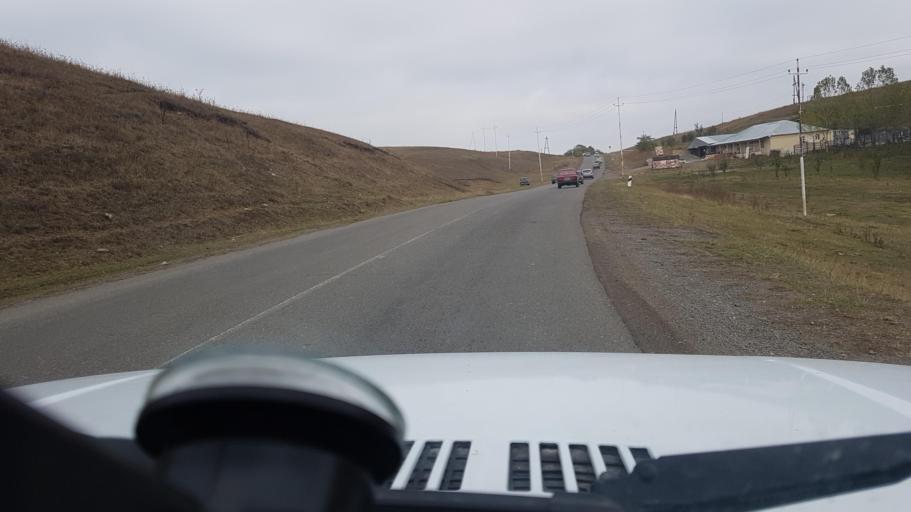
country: AZ
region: Gadabay Rayon
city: Ariqdam
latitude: 40.6172
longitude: 45.8105
